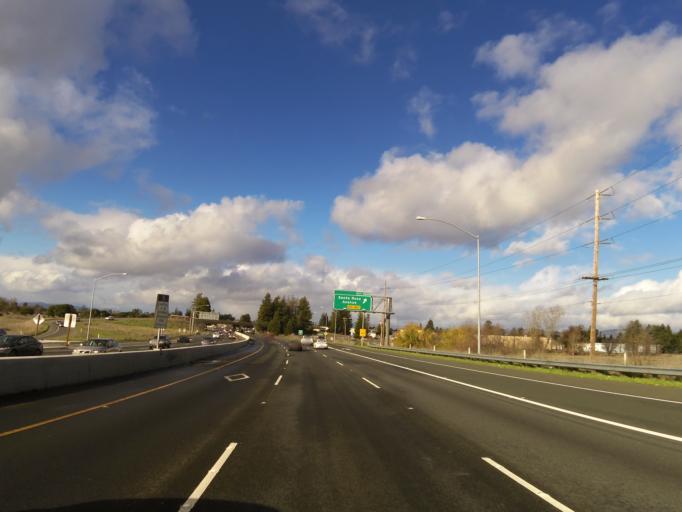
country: US
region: California
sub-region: Sonoma County
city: Rohnert Park
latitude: 38.3693
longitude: -122.7125
